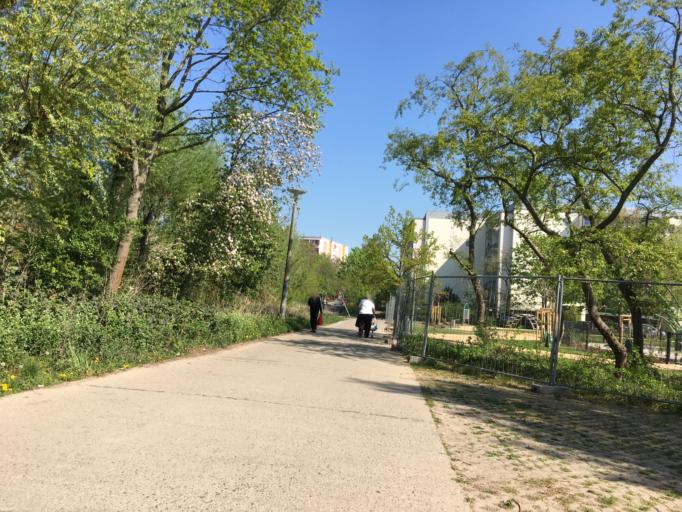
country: DE
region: Berlin
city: Buch
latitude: 52.6309
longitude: 13.4925
